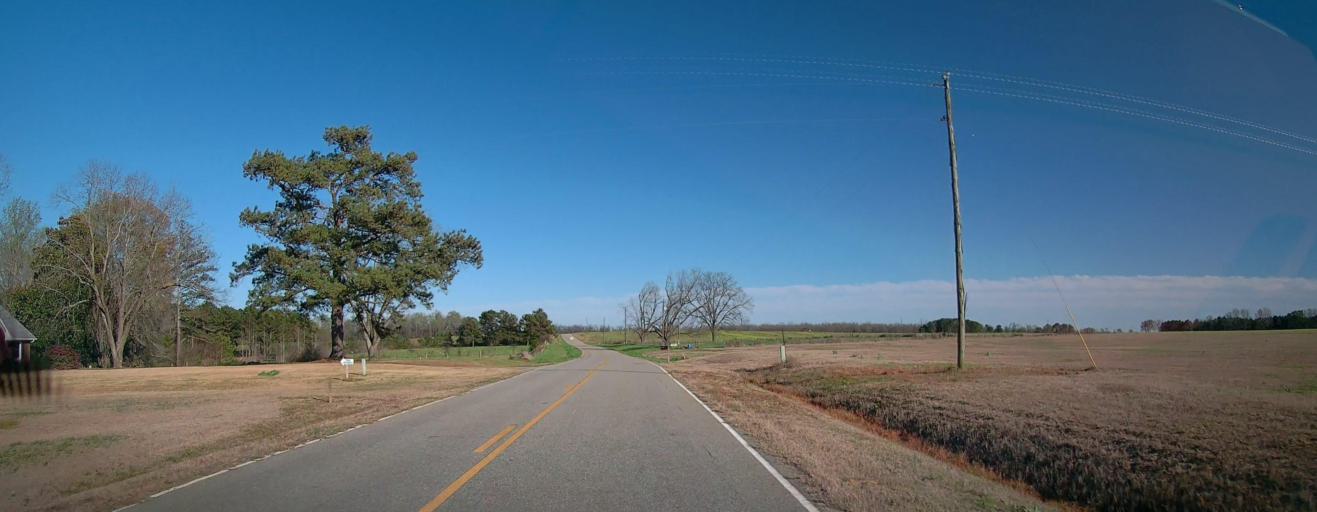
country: US
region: Georgia
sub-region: Houston County
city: Perry
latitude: 32.3694
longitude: -83.7005
